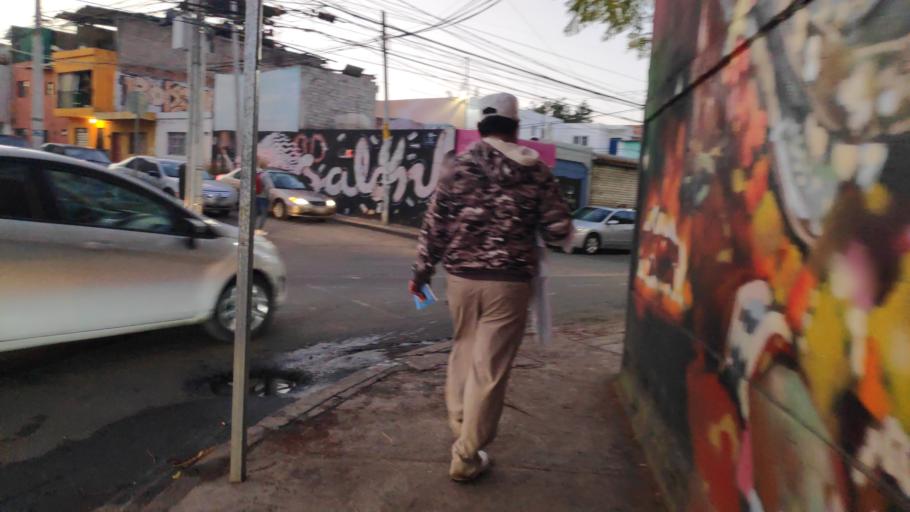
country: MX
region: Queretaro
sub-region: Queretaro
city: Santiago de Queretaro
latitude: 20.5883
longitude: -100.3764
